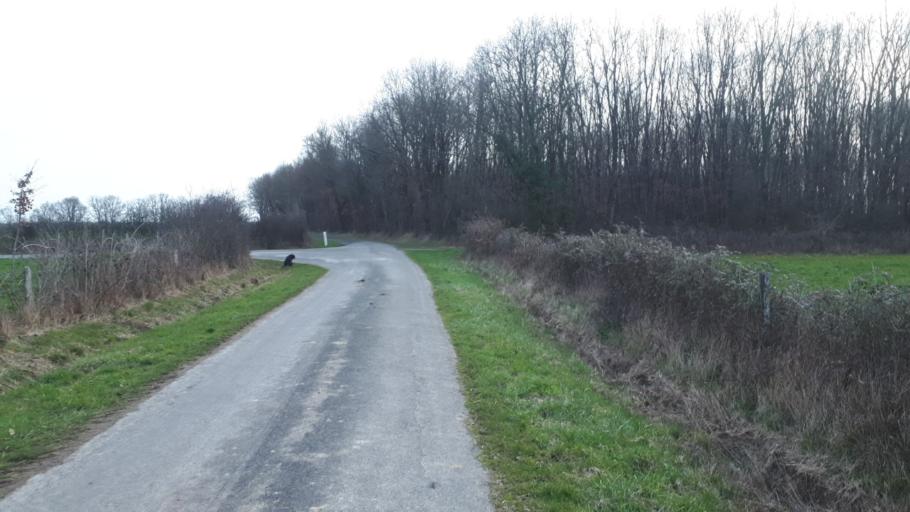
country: FR
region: Poitou-Charentes
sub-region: Departement de la Vienne
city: Archigny
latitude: 46.6214
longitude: 0.7454
